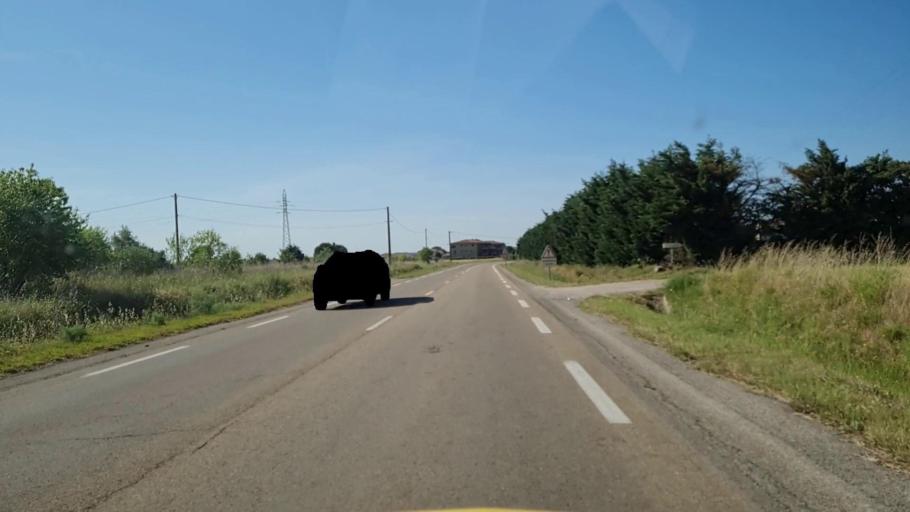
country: FR
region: Languedoc-Roussillon
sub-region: Departement du Gard
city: Saint-Gilles
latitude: 43.7013
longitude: 4.4237
